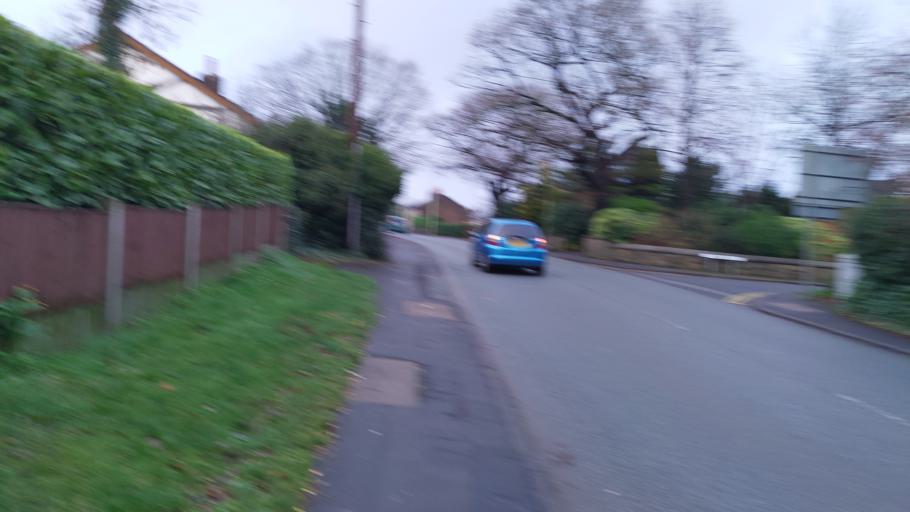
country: GB
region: England
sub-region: Lancashire
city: Euxton
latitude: 53.6715
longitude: -2.6767
